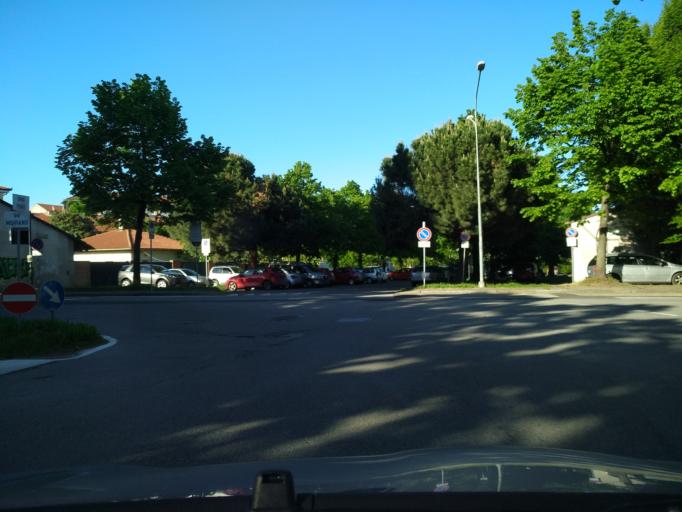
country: IT
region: Piedmont
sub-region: Provincia di Torino
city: Pinerolo
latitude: 44.8830
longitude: 7.3360
